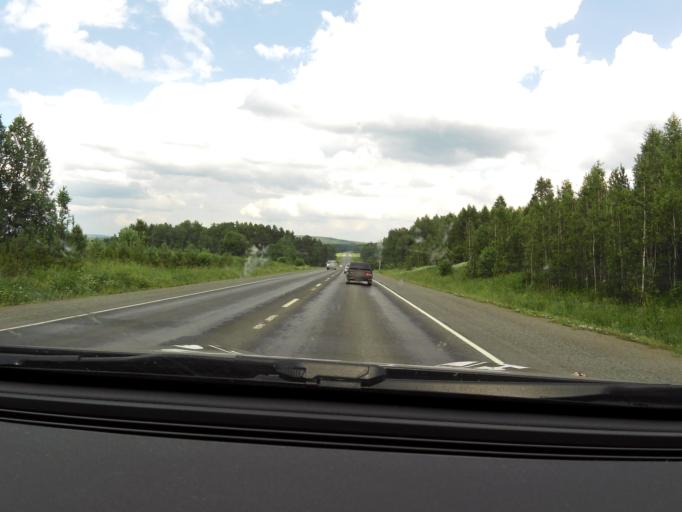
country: RU
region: Sverdlovsk
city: Bisert'
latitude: 56.8178
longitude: 58.7527
